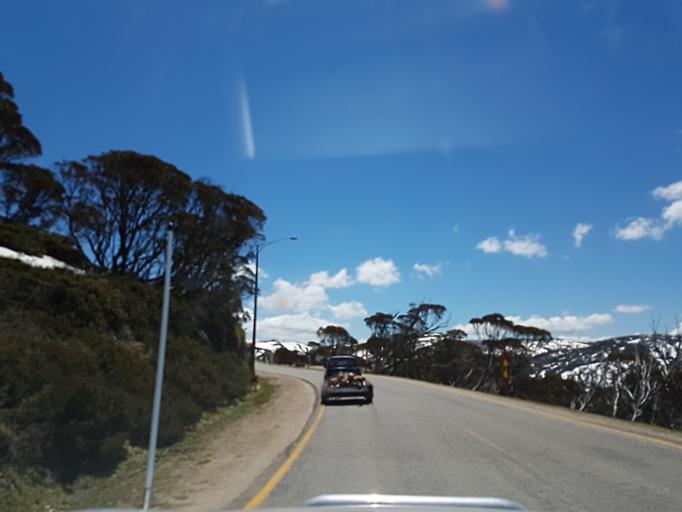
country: AU
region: Victoria
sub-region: Alpine
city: Mount Beauty
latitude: -36.9898
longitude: 147.1486
